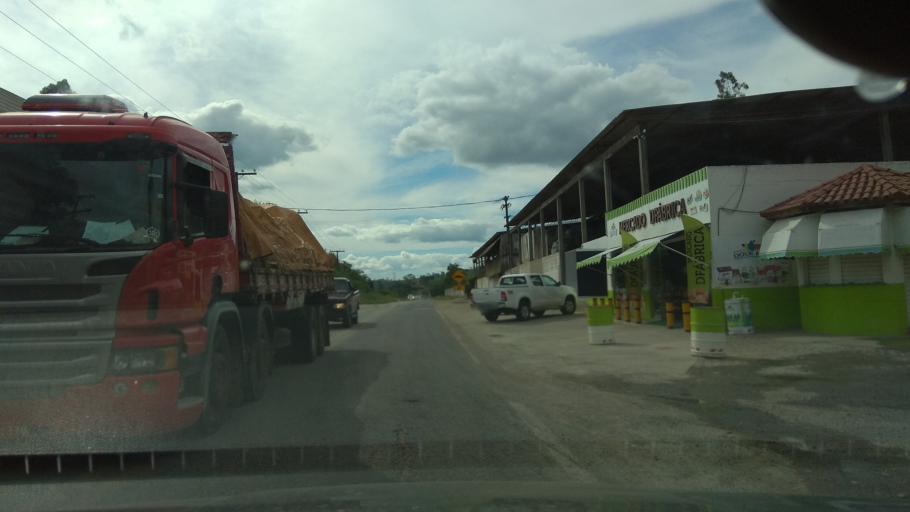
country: BR
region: Bahia
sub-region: Ipiau
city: Ipiau
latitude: -14.1176
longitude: -39.7718
